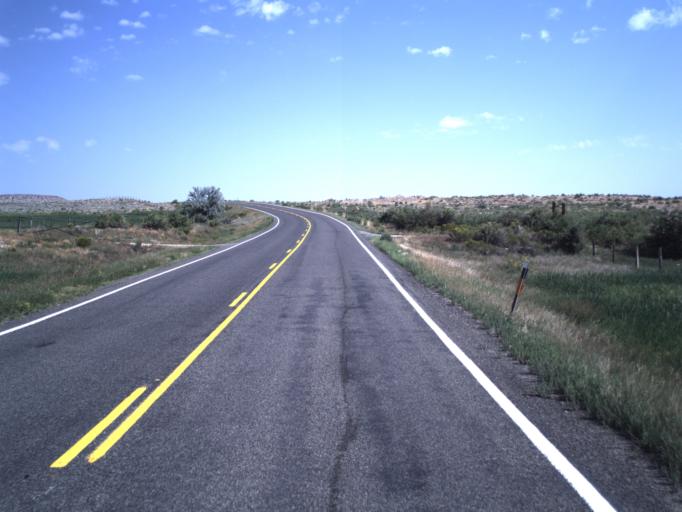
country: US
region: Utah
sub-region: Daggett County
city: Manila
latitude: 40.9657
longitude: -109.7130
